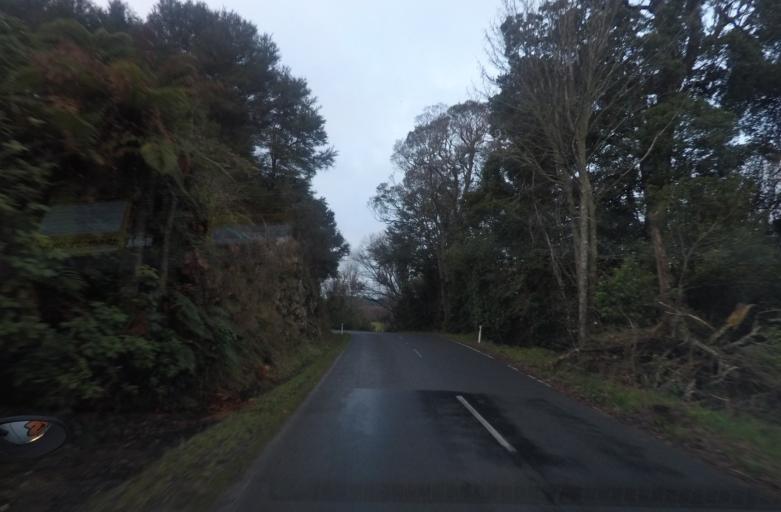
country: NZ
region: Tasman
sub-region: Tasman District
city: Takaka
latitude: -40.8338
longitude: 172.7880
